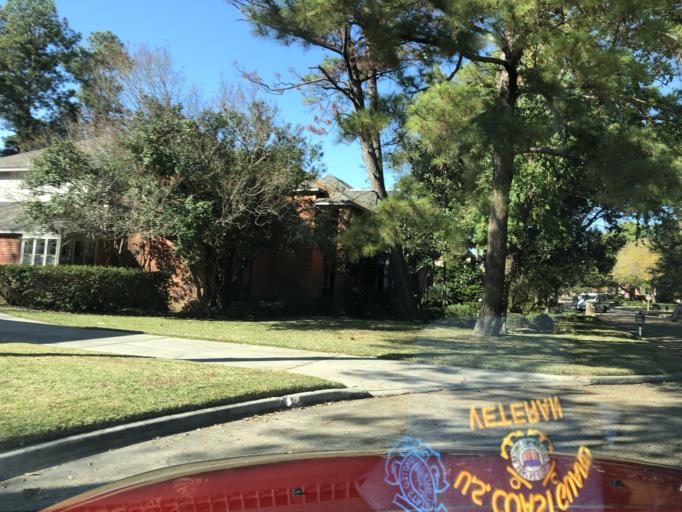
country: US
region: Texas
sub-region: Harris County
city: Tomball
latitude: 30.0233
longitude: -95.5405
